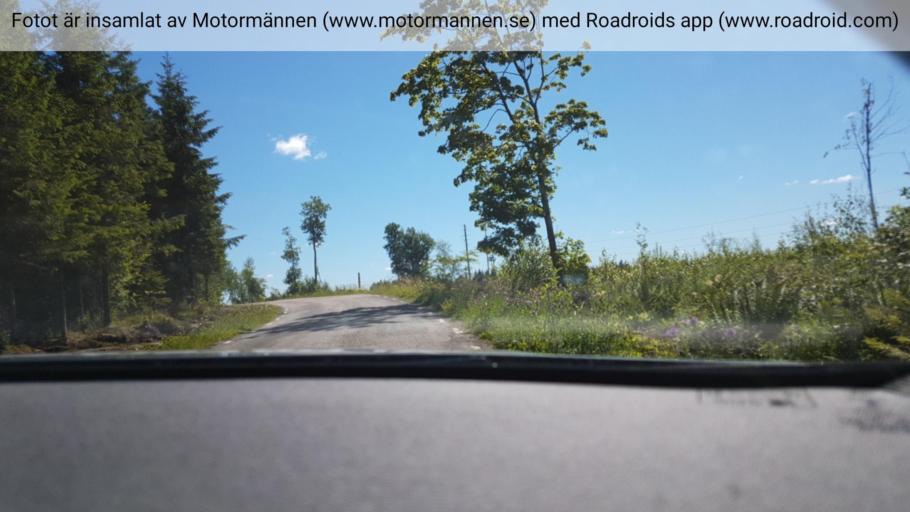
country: SE
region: Vaestra Goetaland
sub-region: Falkopings Kommun
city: Akarp
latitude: 58.1866
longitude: 13.7729
